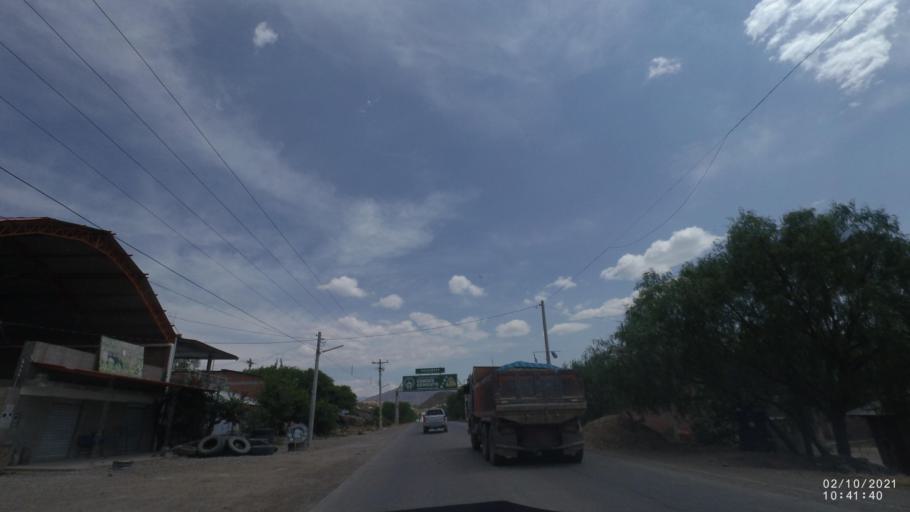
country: BO
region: Cochabamba
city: Capinota
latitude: -17.6125
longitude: -66.2917
